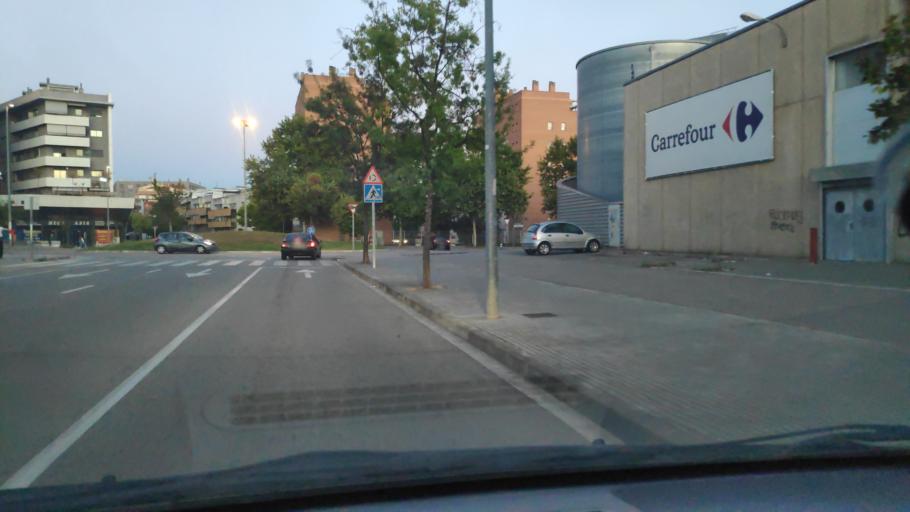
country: ES
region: Catalonia
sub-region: Provincia de Barcelona
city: Terrassa
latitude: 41.5659
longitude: 2.0374
